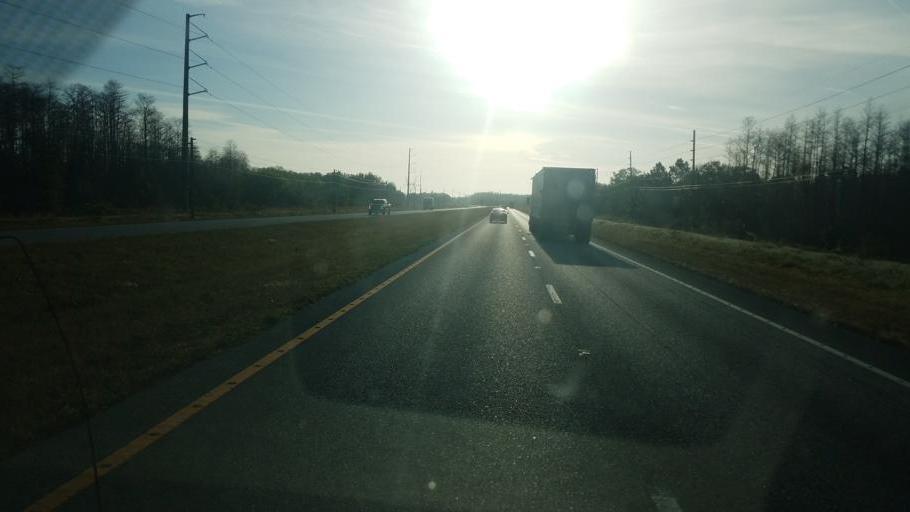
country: US
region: Florida
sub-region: Osceola County
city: Saint Cloud
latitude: 28.1482
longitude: -81.0973
